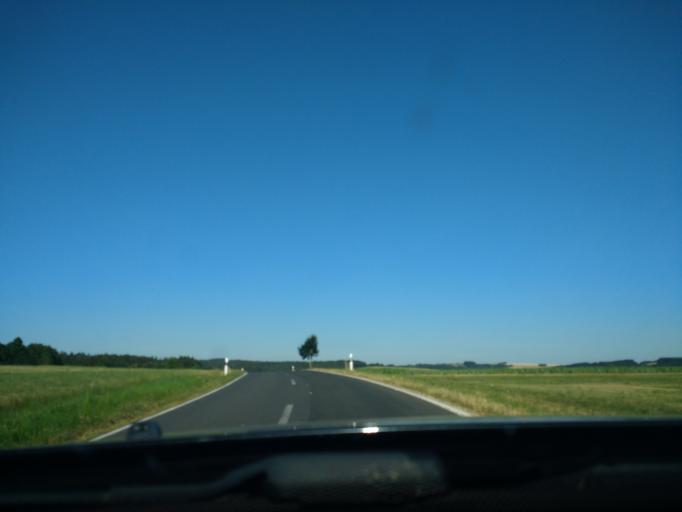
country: DE
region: Rheinland-Pfalz
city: Meisburg
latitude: 50.1079
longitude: 6.6938
